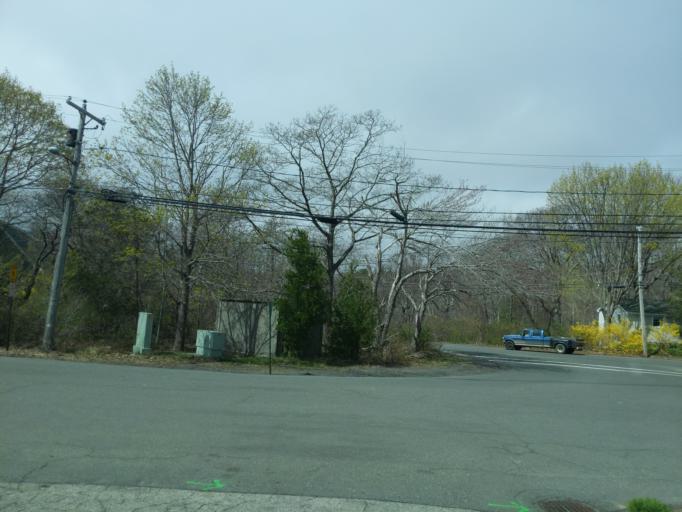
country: US
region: Massachusetts
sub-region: Essex County
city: Rockport
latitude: 42.6410
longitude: -70.6001
